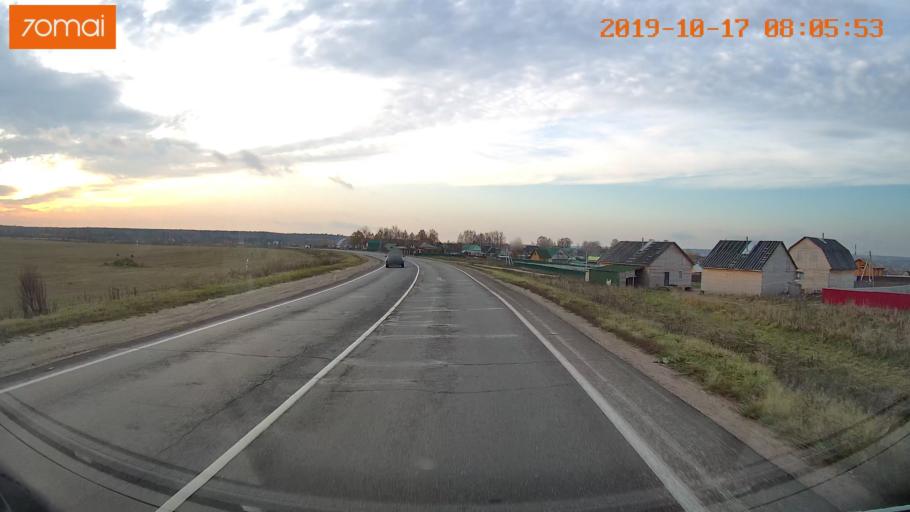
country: RU
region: Vladimir
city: Kol'chugino
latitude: 56.3296
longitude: 39.4108
